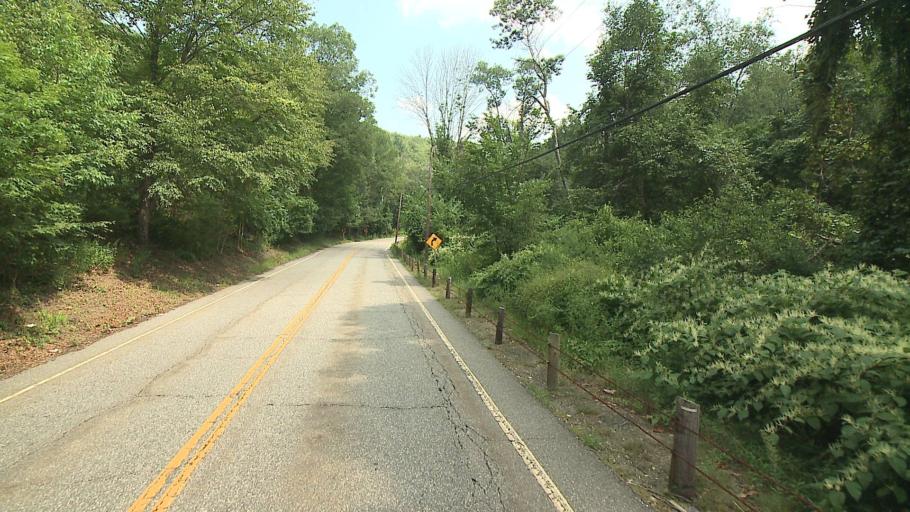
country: US
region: Connecticut
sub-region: Litchfield County
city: Oakville
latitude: 41.6218
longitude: -73.0613
